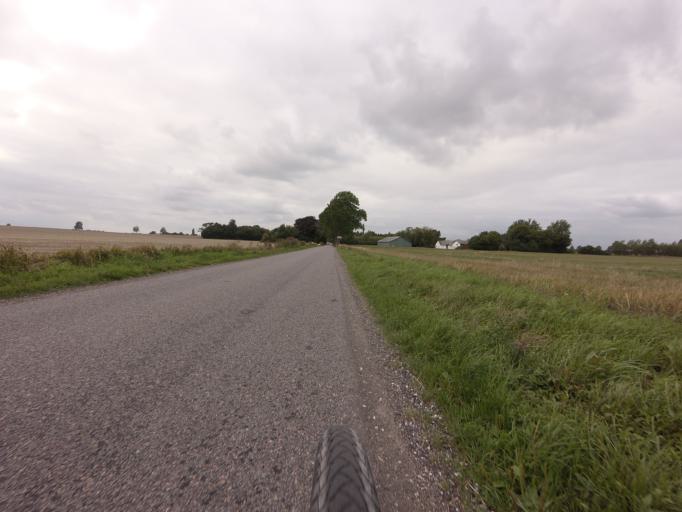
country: DK
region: Zealand
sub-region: Stevns Kommune
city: Store Heddinge
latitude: 55.3402
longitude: 12.4190
